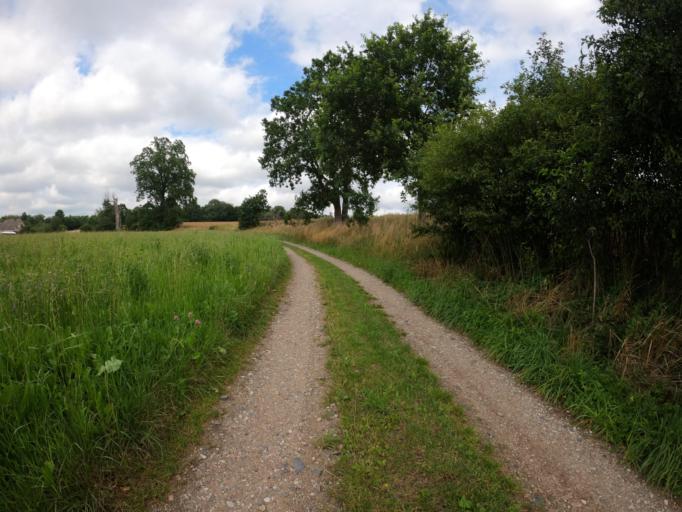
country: PL
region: West Pomeranian Voivodeship
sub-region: Powiat szczecinecki
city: Grzmiaca
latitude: 53.8004
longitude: 16.4731
